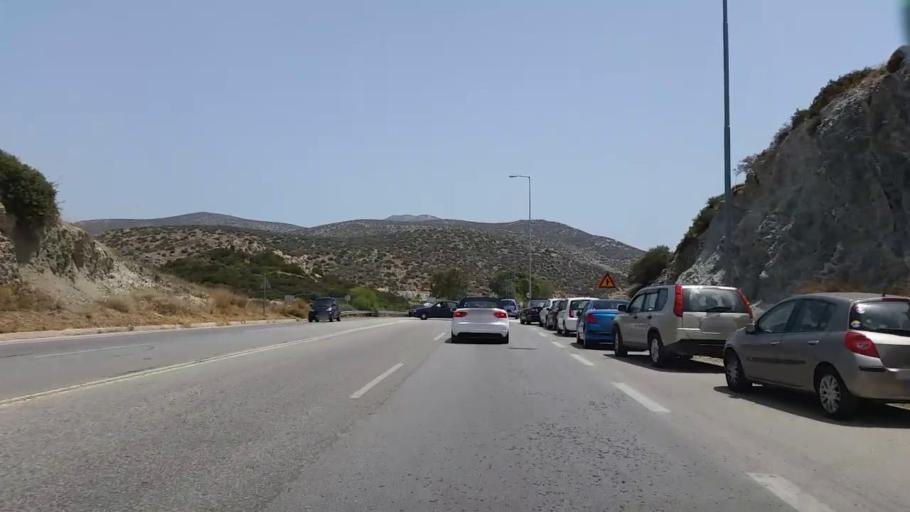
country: GR
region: Attica
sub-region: Nomarchia Anatolikis Attikis
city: Saronida
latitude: 37.7775
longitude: 23.8981
